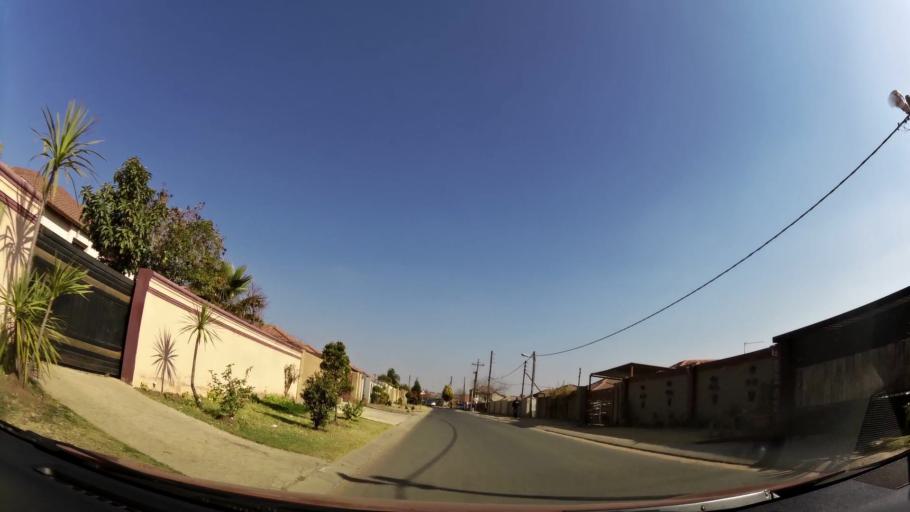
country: ZA
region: Gauteng
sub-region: West Rand District Municipality
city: Muldersdriseloop
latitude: -26.0405
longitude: 27.9202
